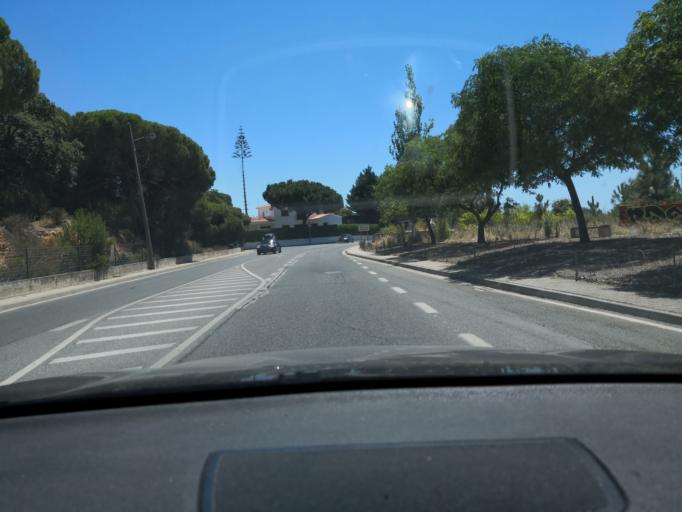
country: PT
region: Faro
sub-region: Albufeira
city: Ferreiras
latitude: 37.1079
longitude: -8.2012
